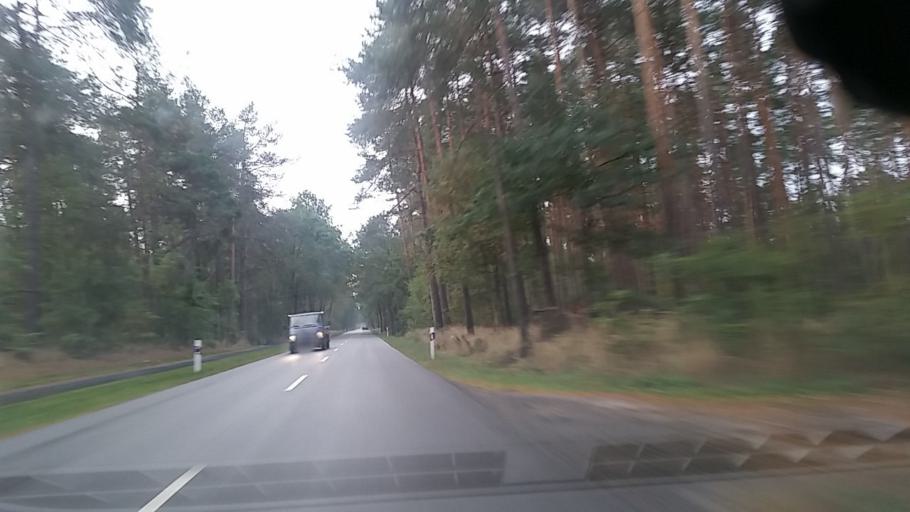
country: DE
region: Lower Saxony
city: Bokensdorf
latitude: 52.5194
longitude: 10.7162
